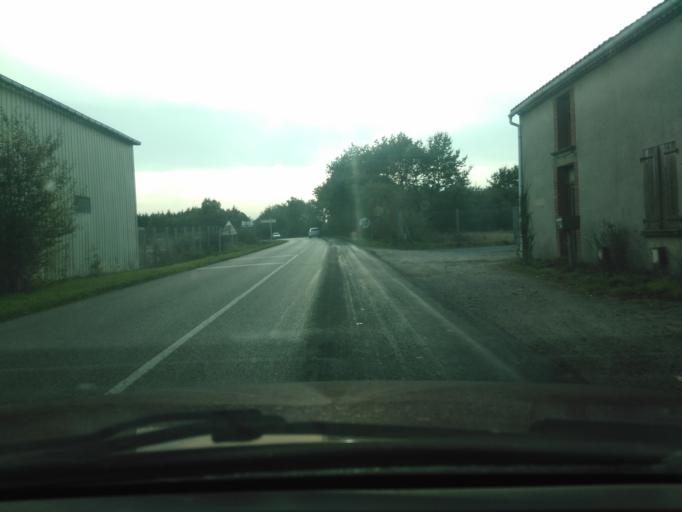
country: FR
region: Pays de la Loire
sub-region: Departement de la Vendee
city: Dompierre-sur-Yon
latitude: 46.7173
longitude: -1.4079
